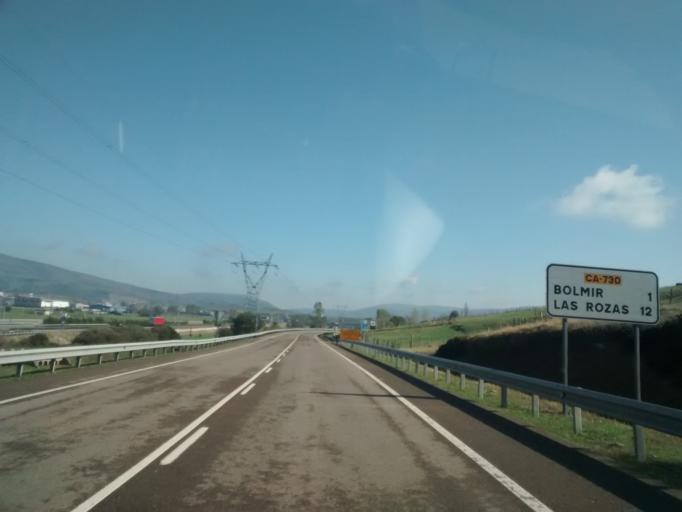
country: ES
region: Cantabria
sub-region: Provincia de Cantabria
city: Reinosa
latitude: 42.9864
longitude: -4.1313
